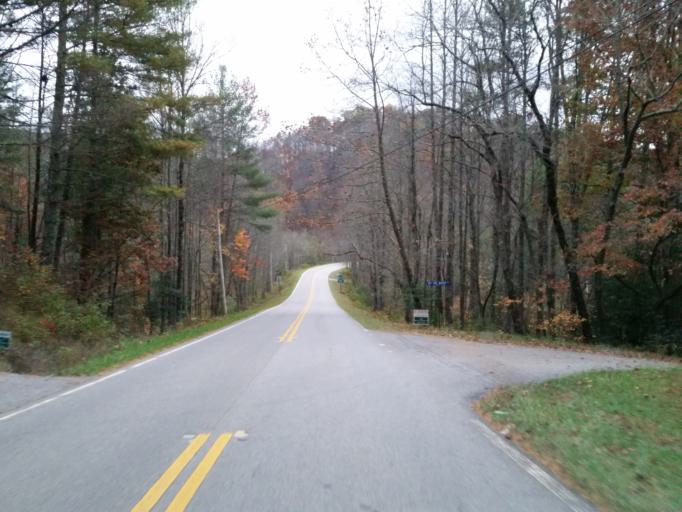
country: US
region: Georgia
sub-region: Union County
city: Blairsville
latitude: 34.7328
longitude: -84.0807
